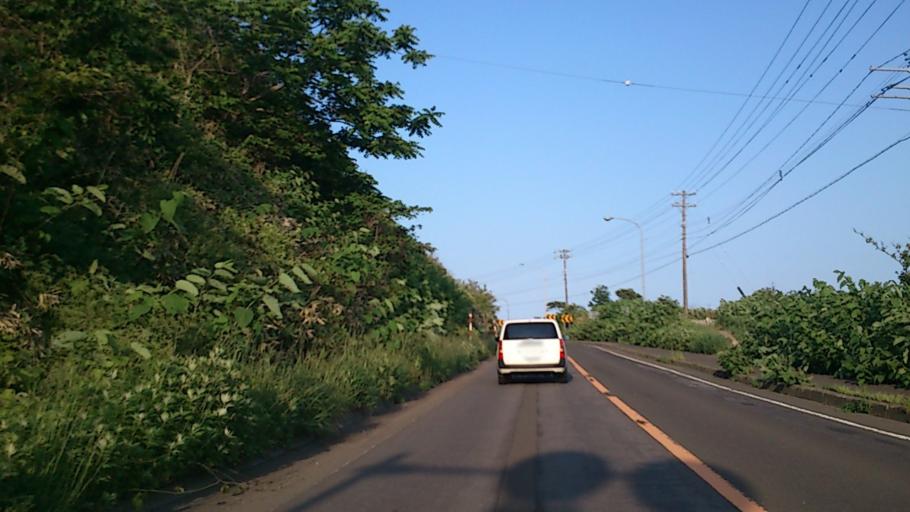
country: JP
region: Hokkaido
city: Kamiiso
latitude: 41.4652
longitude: 140.2506
